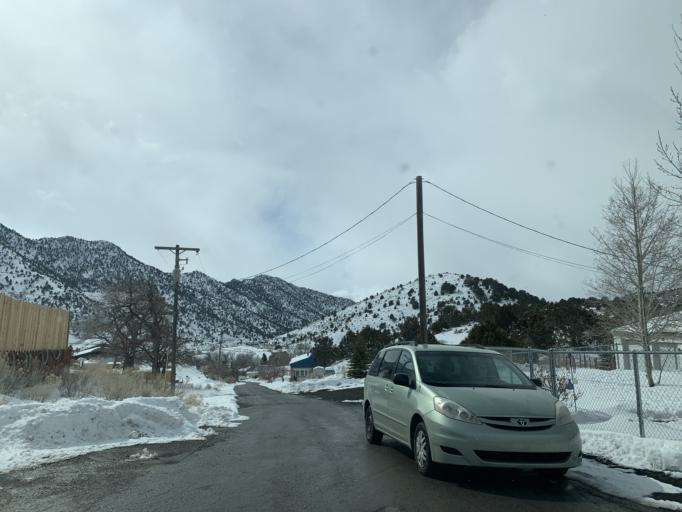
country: US
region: Utah
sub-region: Utah County
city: Genola
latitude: 39.9587
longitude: -112.1219
